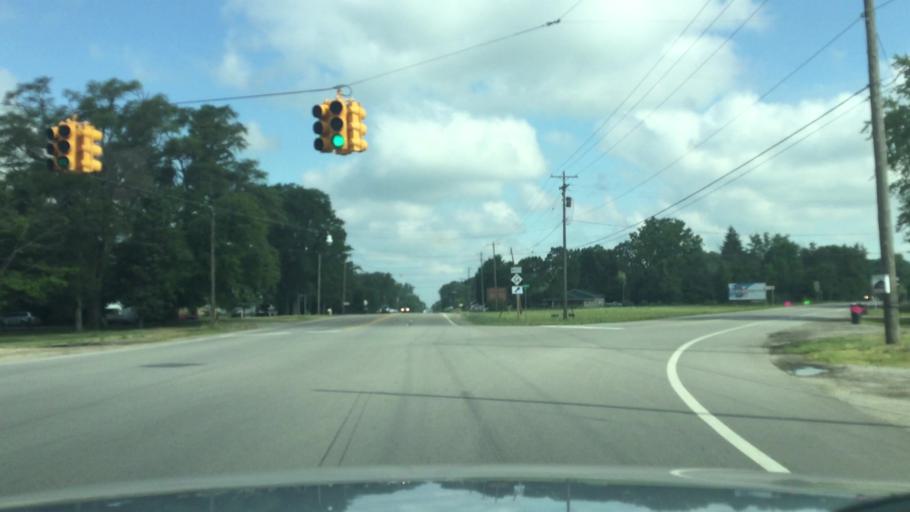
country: US
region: Michigan
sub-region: Genesee County
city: Clio
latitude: 43.2042
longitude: -83.7347
